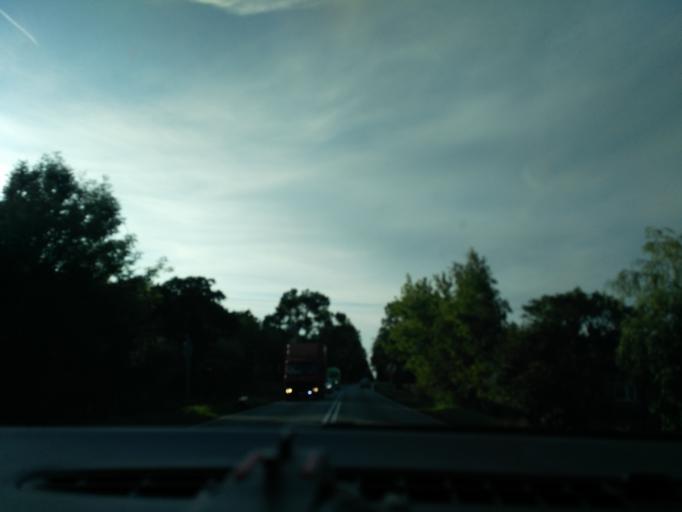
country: PL
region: Lublin Voivodeship
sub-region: Powiat krasnicki
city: Szastarka
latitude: 50.8450
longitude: 22.2939
